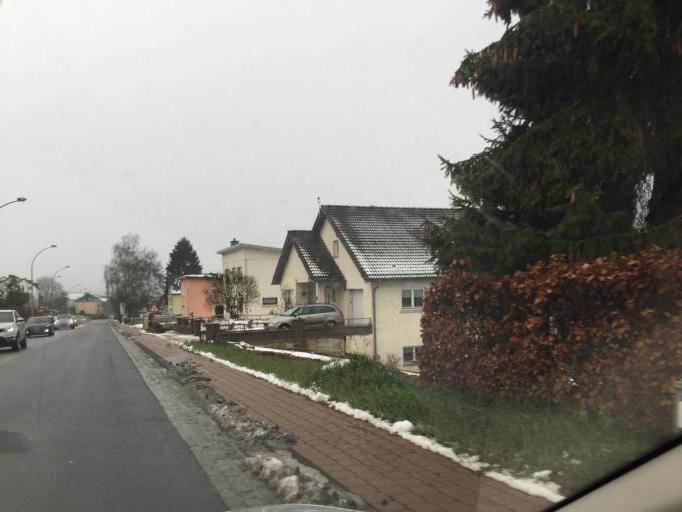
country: LU
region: Diekirch
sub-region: Canton de Diekirch
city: Niederfeulen
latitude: 49.8532
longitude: 6.0545
